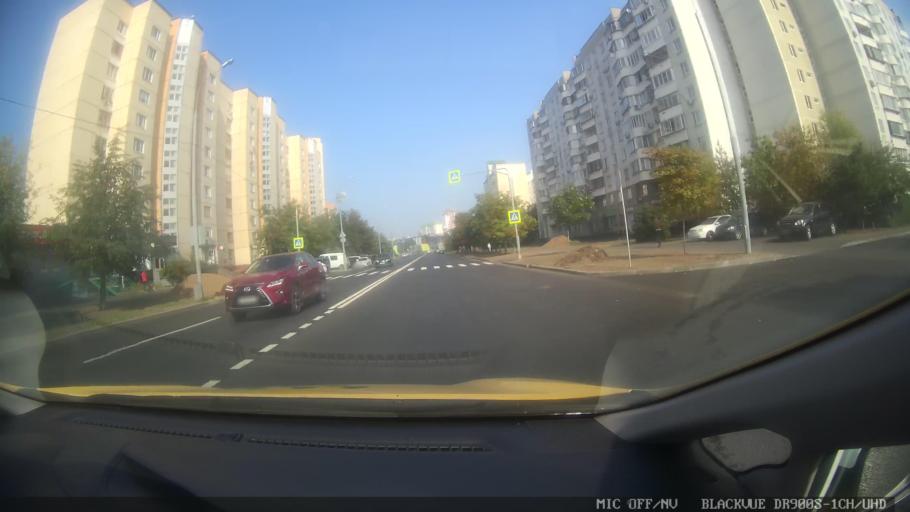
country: RU
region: Moscow
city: Zhulebino
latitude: 55.6819
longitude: 37.8564
